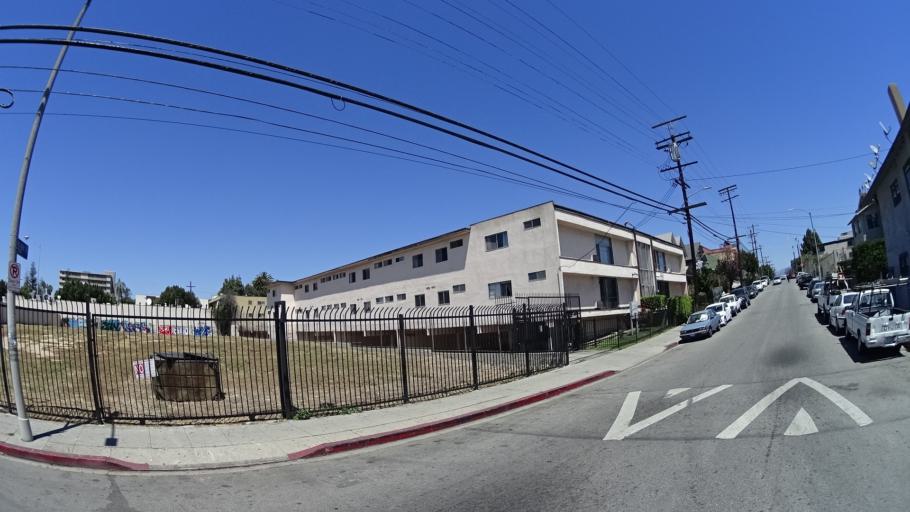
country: US
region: California
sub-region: Los Angeles County
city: Echo Park
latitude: 34.0621
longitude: -118.2684
